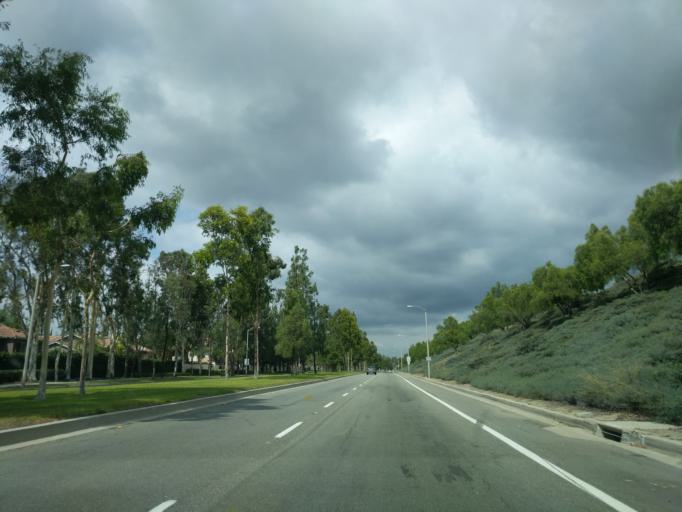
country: US
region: California
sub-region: Orange County
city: North Tustin
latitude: 33.7537
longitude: -117.7655
